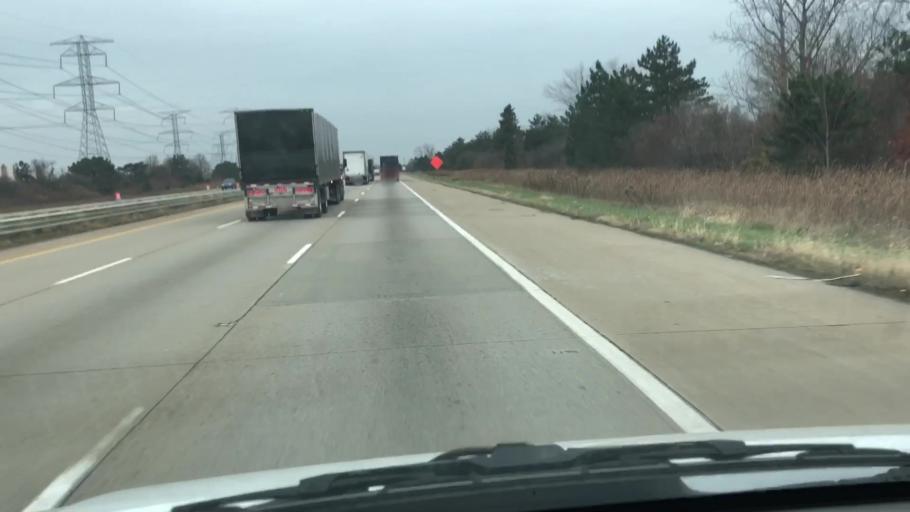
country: US
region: Michigan
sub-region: Monroe County
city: South Rockwood
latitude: 42.0434
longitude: -83.2808
